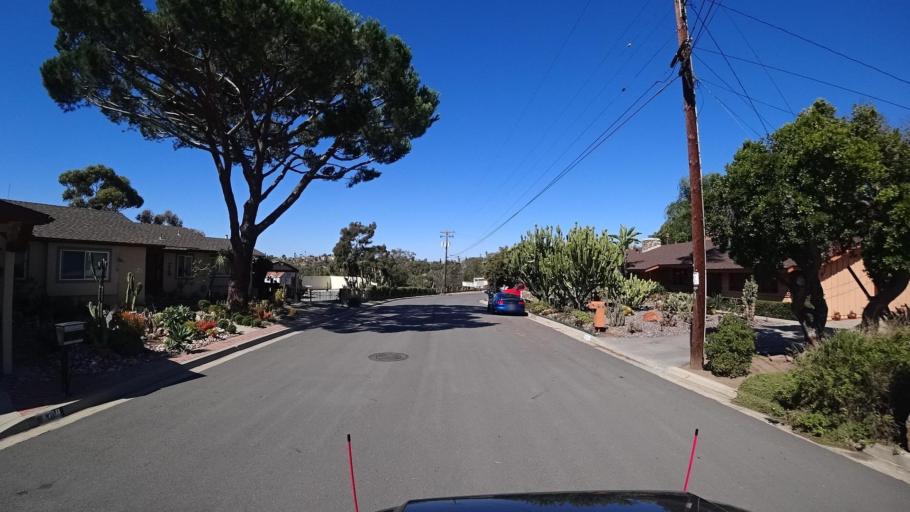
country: US
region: California
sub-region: San Diego County
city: Chula Vista
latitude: 32.6555
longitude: -117.0632
